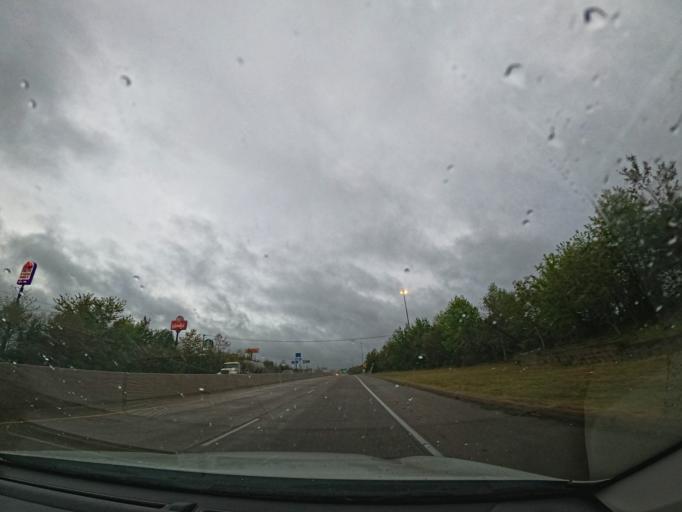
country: US
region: Texas
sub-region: Angelina County
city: Lufkin
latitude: 31.2984
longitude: -94.7277
